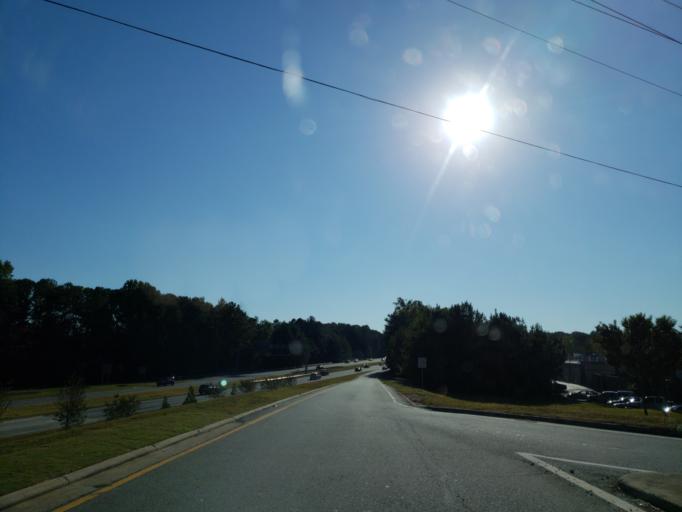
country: US
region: Georgia
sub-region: Gwinnett County
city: Lawrenceville
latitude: 33.9672
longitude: -84.0177
